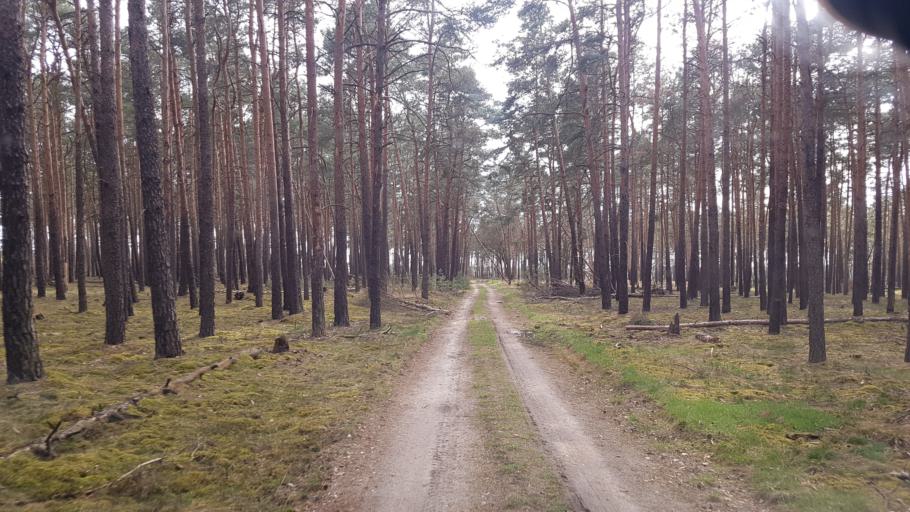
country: DE
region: Brandenburg
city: Schlieben
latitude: 51.6737
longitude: 13.4361
